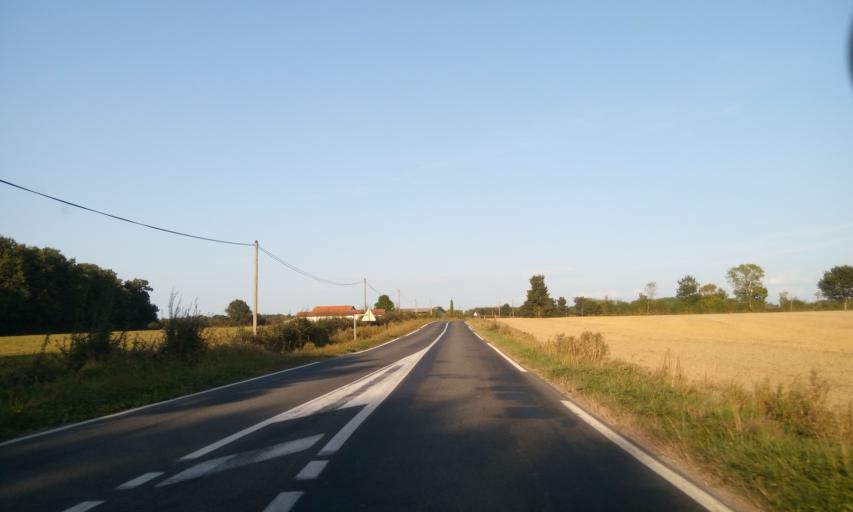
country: FR
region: Rhone-Alpes
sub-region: Departement de l'Ain
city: Chalamont
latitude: 45.9954
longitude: 5.1332
